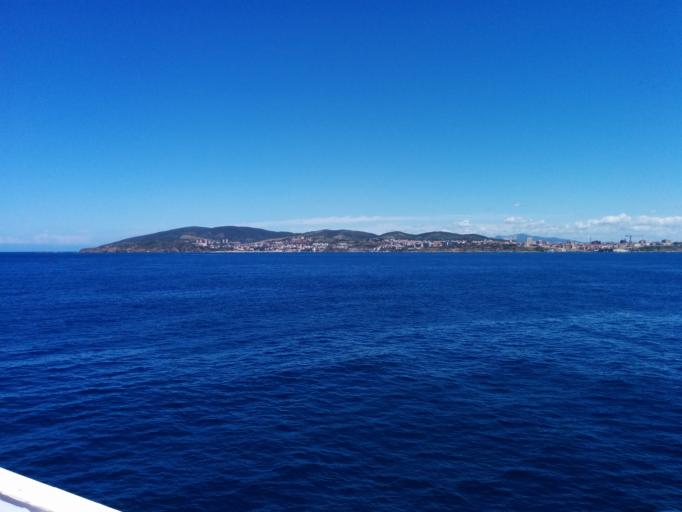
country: IT
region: Tuscany
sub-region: Provincia di Livorno
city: Piombino
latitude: 42.8999
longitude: 10.5088
